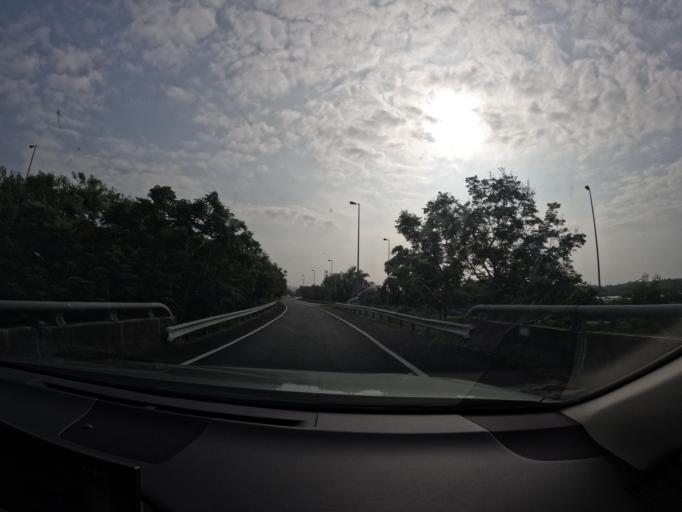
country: TW
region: Taiwan
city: Yujing
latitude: 23.1671
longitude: 120.3544
